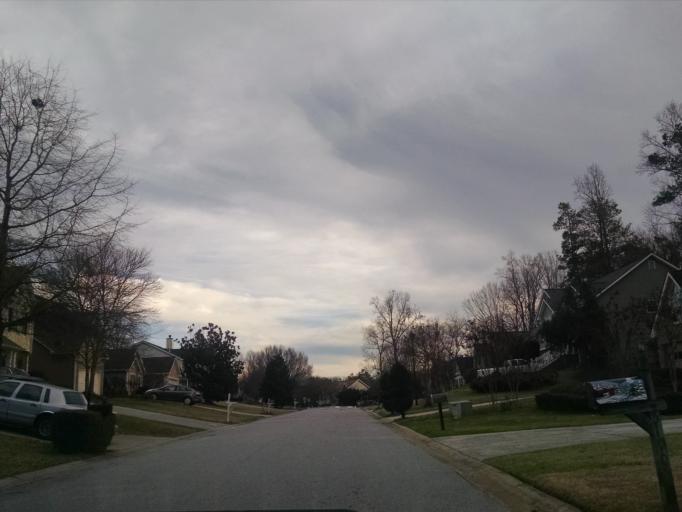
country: US
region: Georgia
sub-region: Gwinnett County
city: Sugar Hill
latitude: 34.1073
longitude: -84.0536
